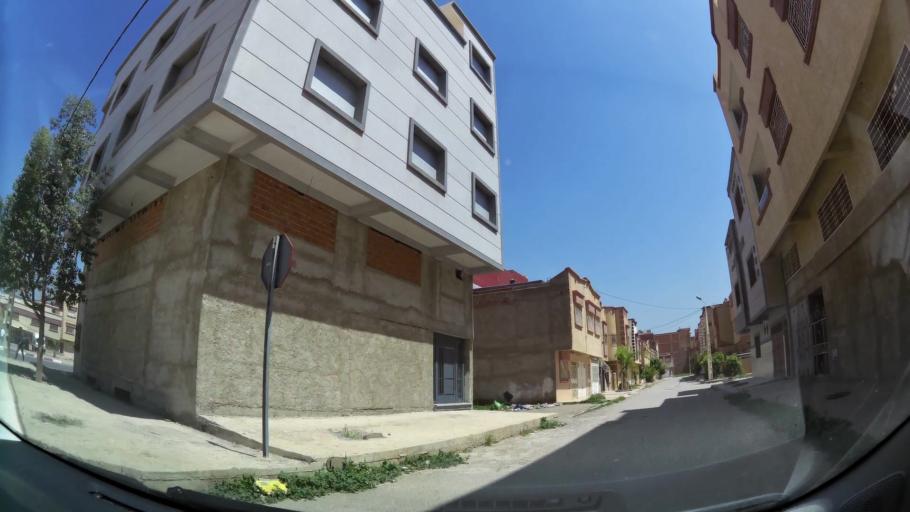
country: MA
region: Oriental
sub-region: Oujda-Angad
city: Oujda
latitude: 34.6957
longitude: -1.8828
